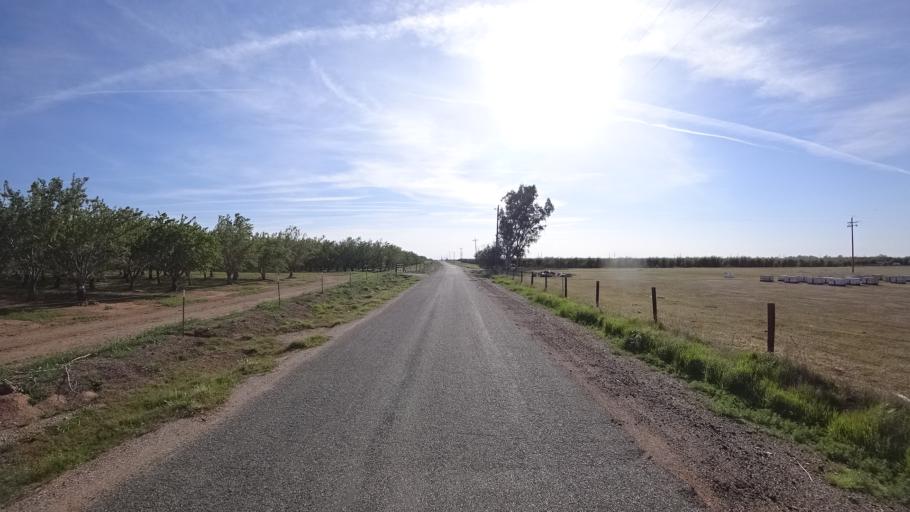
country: US
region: California
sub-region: Glenn County
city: Orland
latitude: 39.6688
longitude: -122.2915
